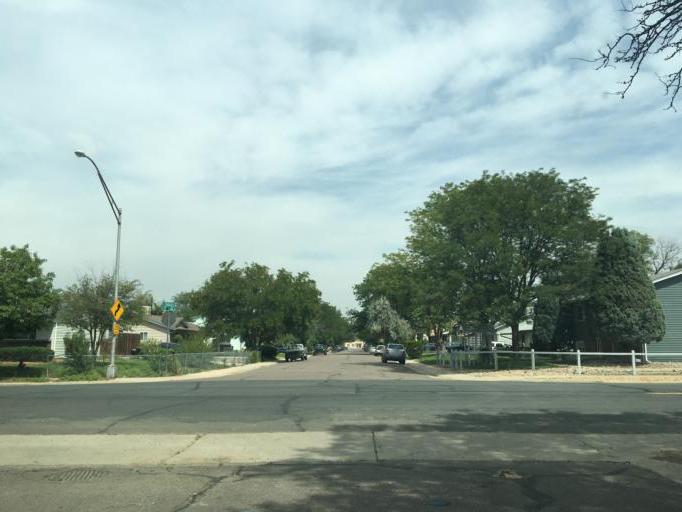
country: US
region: Colorado
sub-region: Adams County
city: Aurora
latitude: 39.7327
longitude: -104.7931
